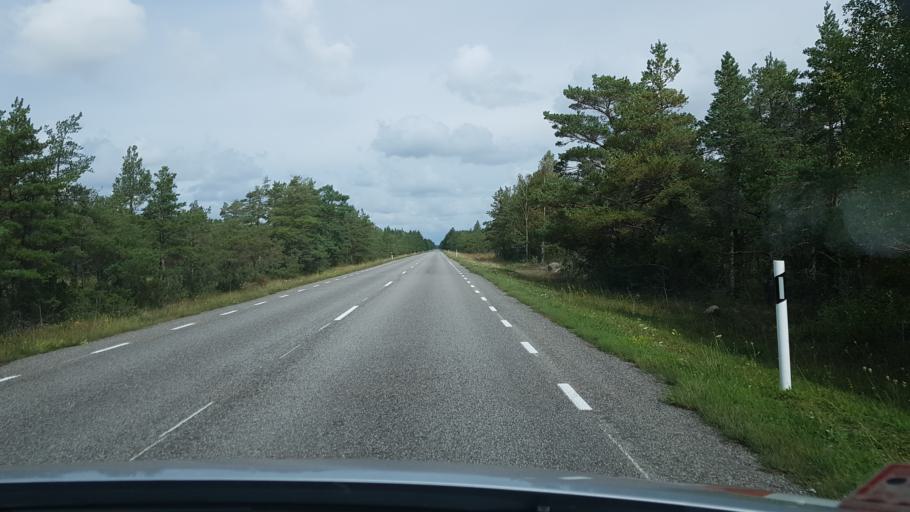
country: EE
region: Saare
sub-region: Kuressaare linn
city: Kuressaare
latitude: 58.4263
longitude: 21.9915
